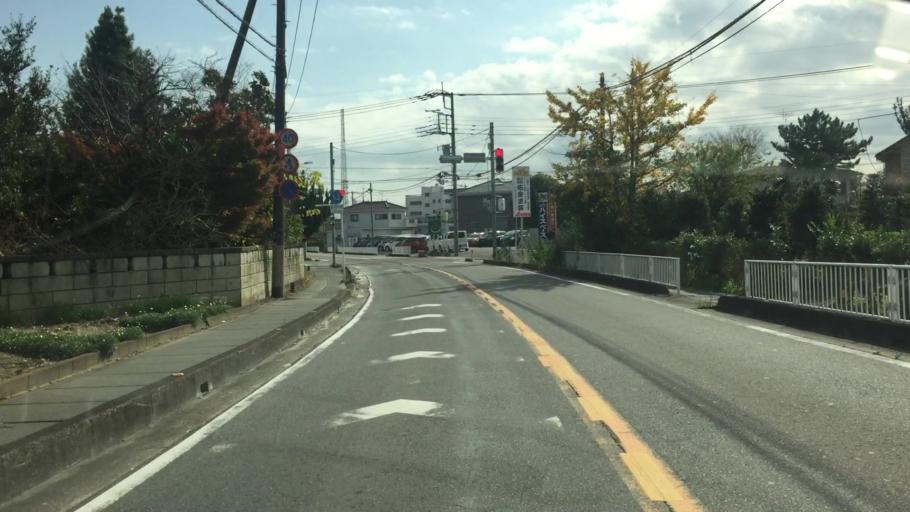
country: JP
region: Saitama
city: Yoshikawa
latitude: 35.8781
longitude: 139.8559
